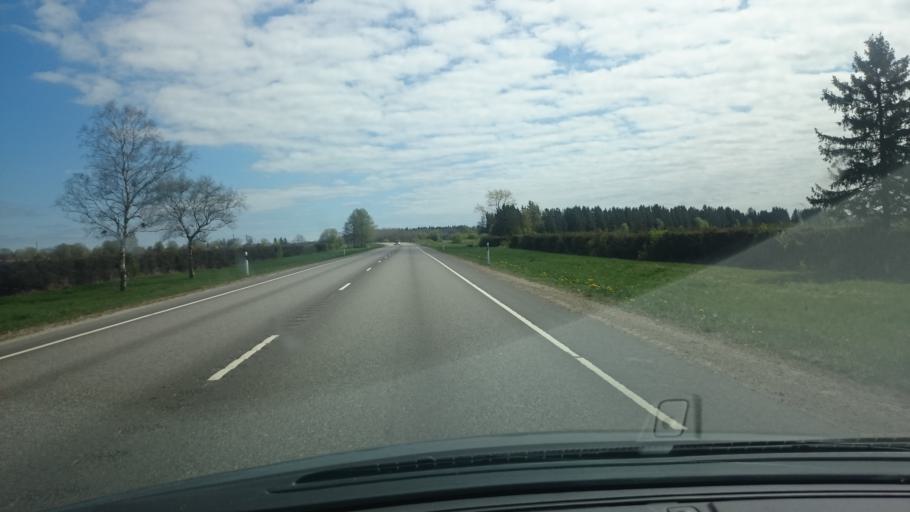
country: EE
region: Ida-Virumaa
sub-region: Kohtla-Nomme vald
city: Kohtla-Nomme
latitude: 59.4215
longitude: 27.1945
